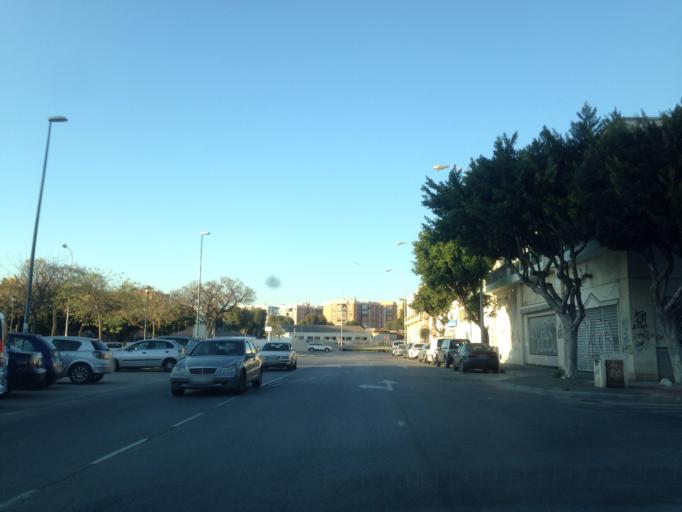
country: ES
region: Andalusia
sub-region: Provincia de Malaga
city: Malaga
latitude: 36.6875
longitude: -4.4474
